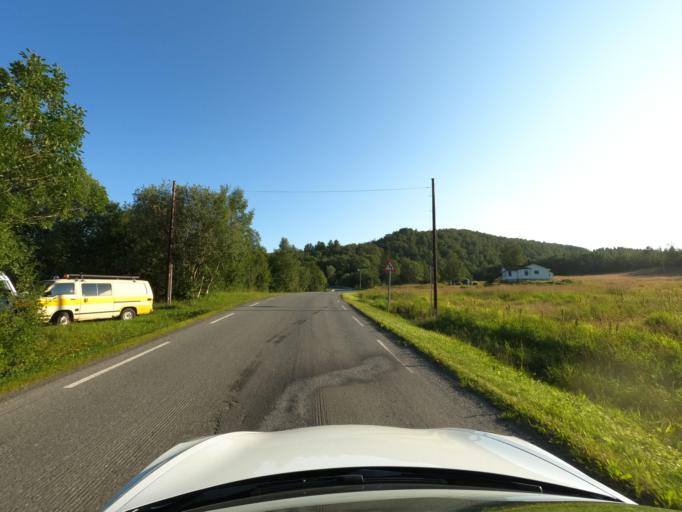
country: NO
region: Nordland
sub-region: Evenes
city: Randa
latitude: 68.4919
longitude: 16.8964
